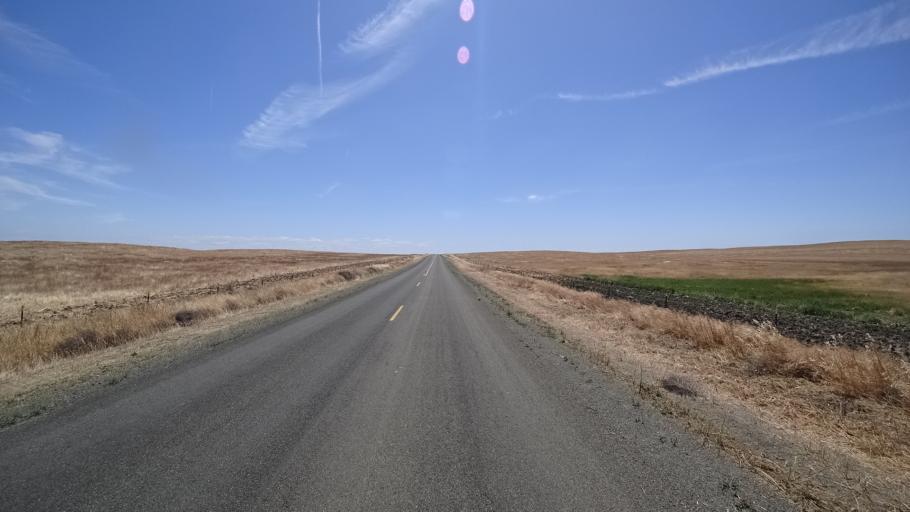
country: US
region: California
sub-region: Kings County
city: Kettleman City
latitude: 35.8233
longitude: -119.9083
